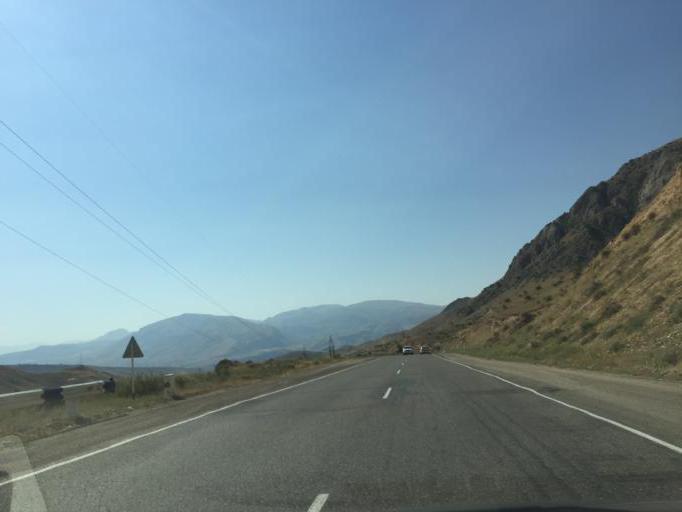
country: AM
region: Vayots' Dzori Marz
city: Rrind
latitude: 39.7785
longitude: 45.1195
